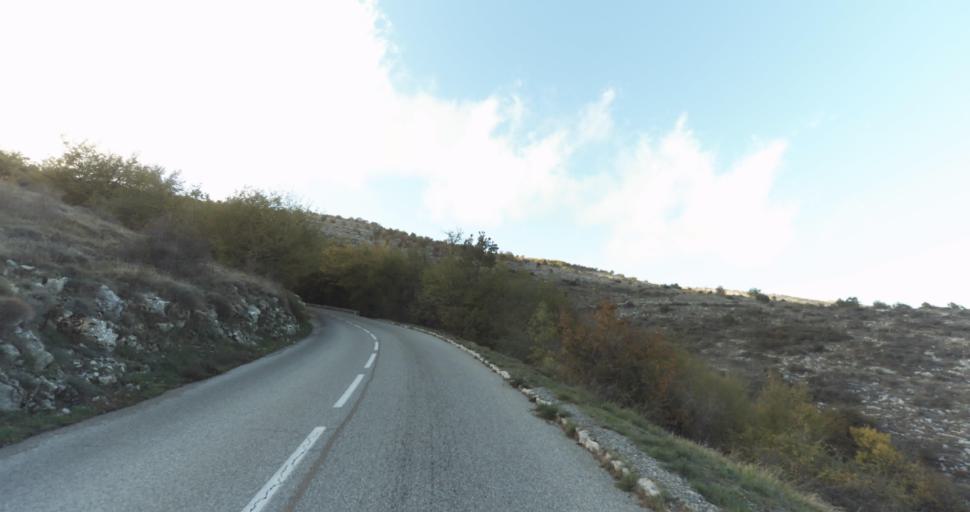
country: FR
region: Provence-Alpes-Cote d'Azur
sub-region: Departement des Alpes-Maritimes
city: Vence
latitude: 43.7561
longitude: 7.0873
